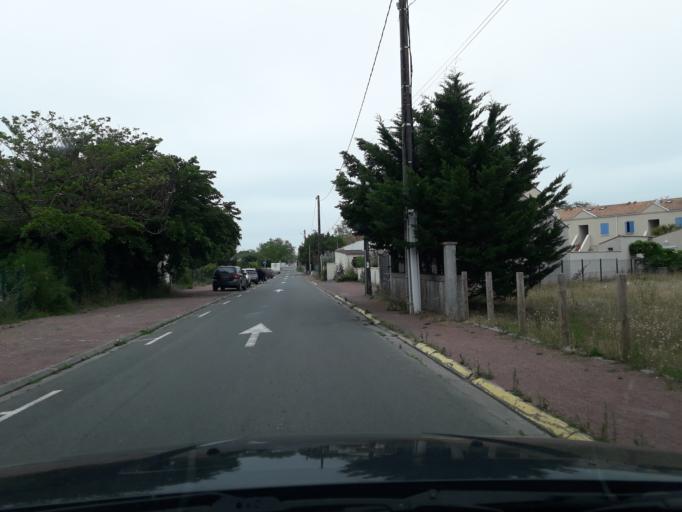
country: FR
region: Poitou-Charentes
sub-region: Departement de la Charente-Maritime
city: Boyard-Ville
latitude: 45.9689
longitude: -1.2416
